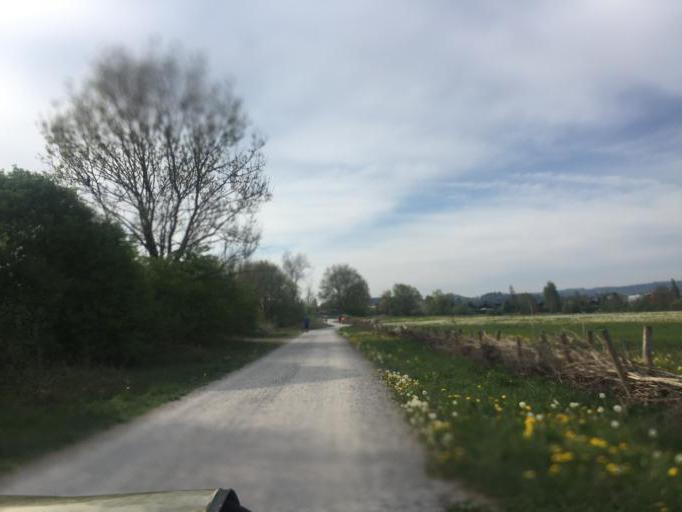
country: CH
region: Bern
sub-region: Bern-Mittelland District
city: Rubigen
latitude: 46.8900
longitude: 7.5463
